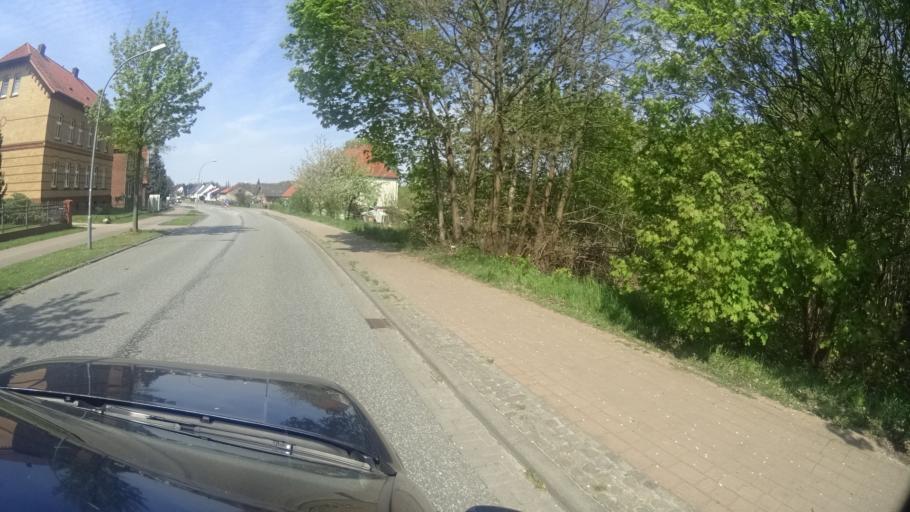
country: DE
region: Brandenburg
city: Wusterhausen
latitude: 52.8547
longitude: 12.4467
